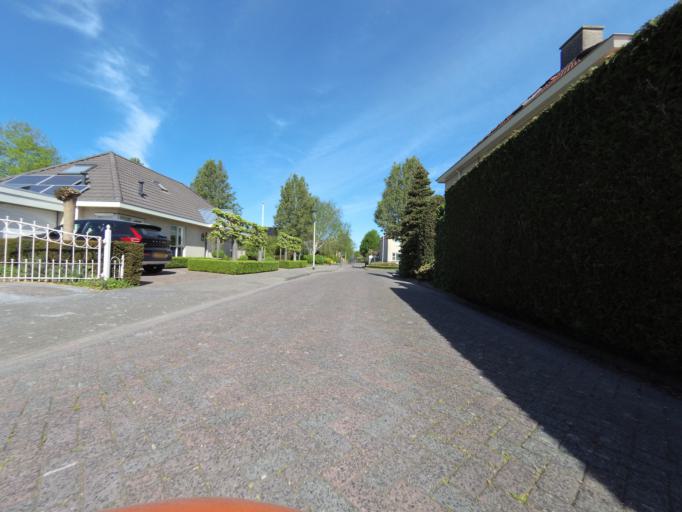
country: NL
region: Flevoland
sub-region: Gemeente Dronten
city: Dronten
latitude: 52.5284
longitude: 5.7028
